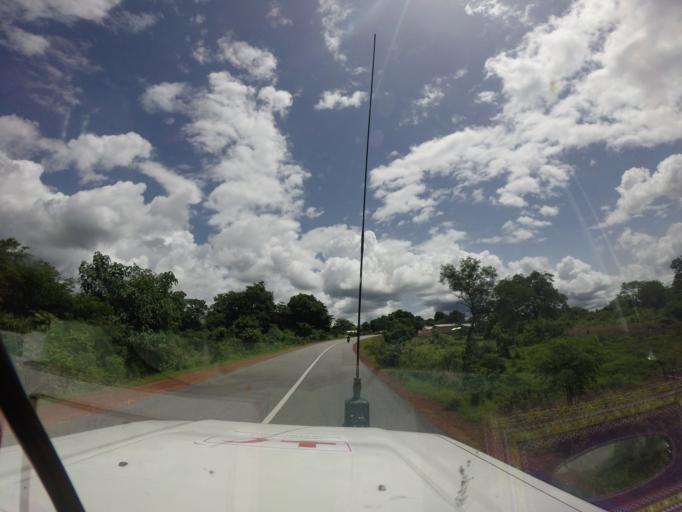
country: SL
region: Northern Province
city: Bindi
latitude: 10.1548
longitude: -11.4421
